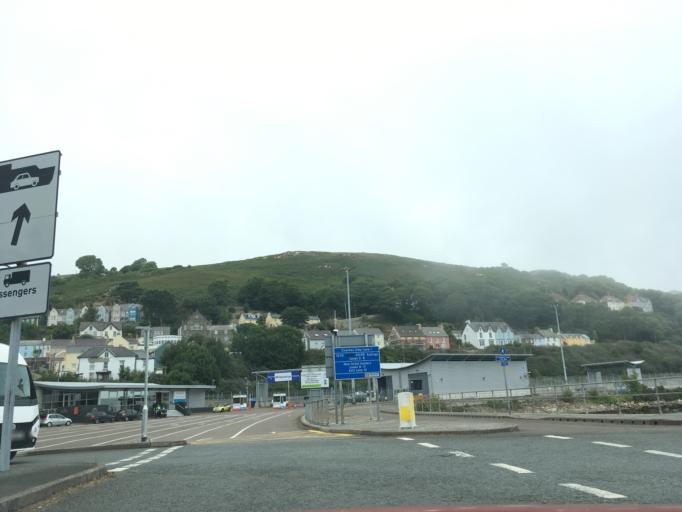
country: GB
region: Wales
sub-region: Pembrokeshire
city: Goodwick
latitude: 52.0037
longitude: -4.9931
